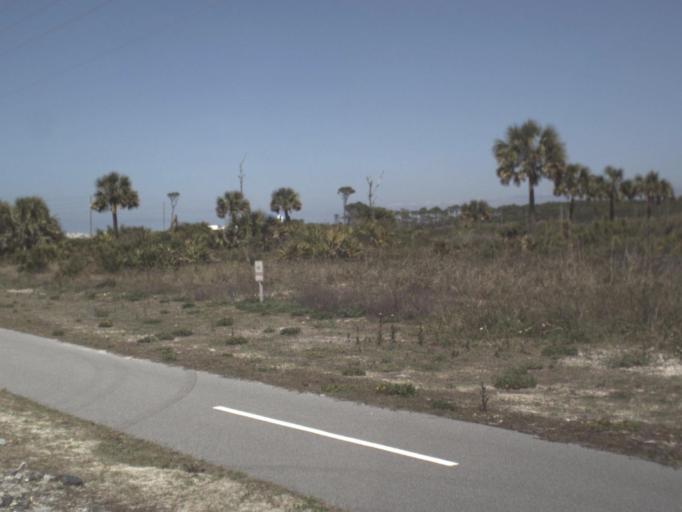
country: US
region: Florida
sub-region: Gulf County
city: Port Saint Joe
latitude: 29.6772
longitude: -85.3639
